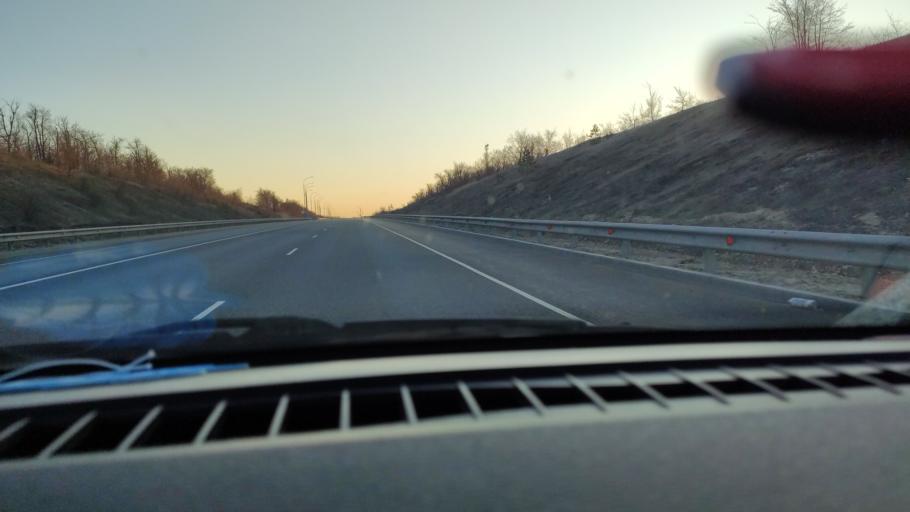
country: RU
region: Saratov
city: Yelshanka
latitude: 51.8899
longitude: 46.5220
